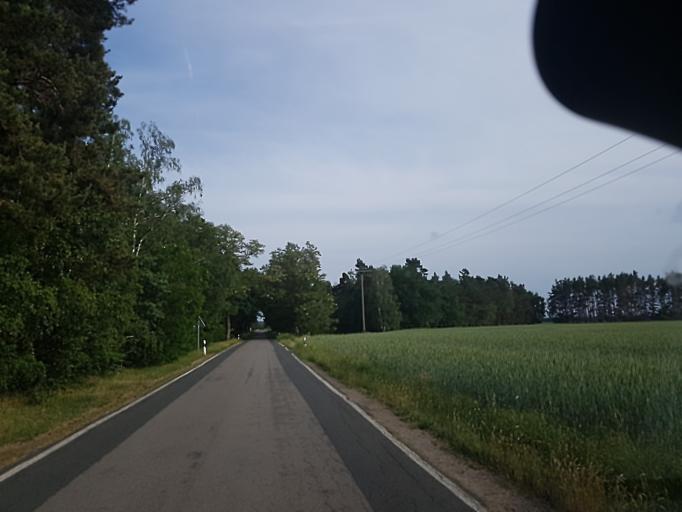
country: DE
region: Saxony-Anhalt
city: Seyda
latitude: 51.8406
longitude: 12.9270
